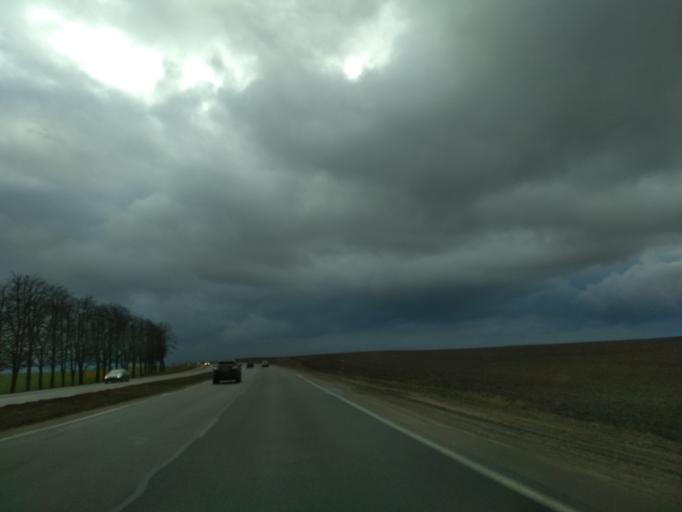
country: BY
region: Minsk
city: Luhavaya Slabada
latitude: 53.7537
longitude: 27.8316
